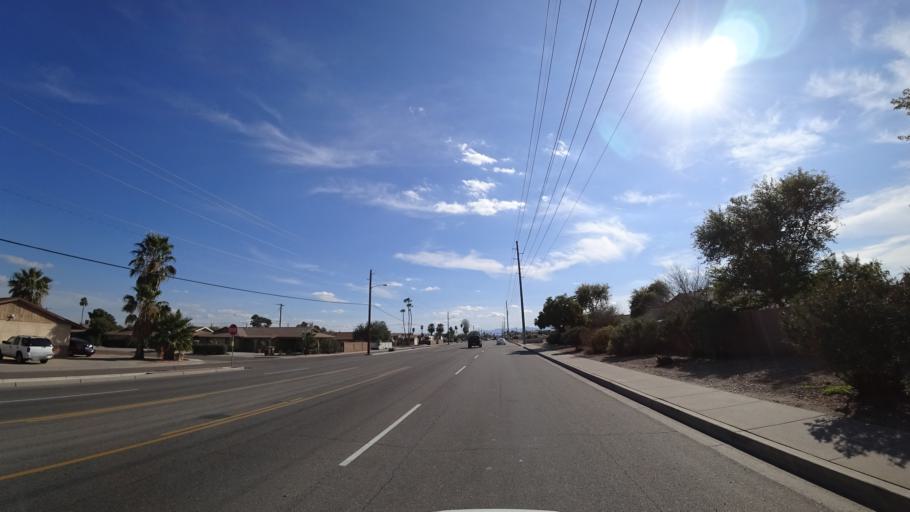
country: US
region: Arizona
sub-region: Maricopa County
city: Peoria
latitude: 33.5846
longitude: -112.2204
